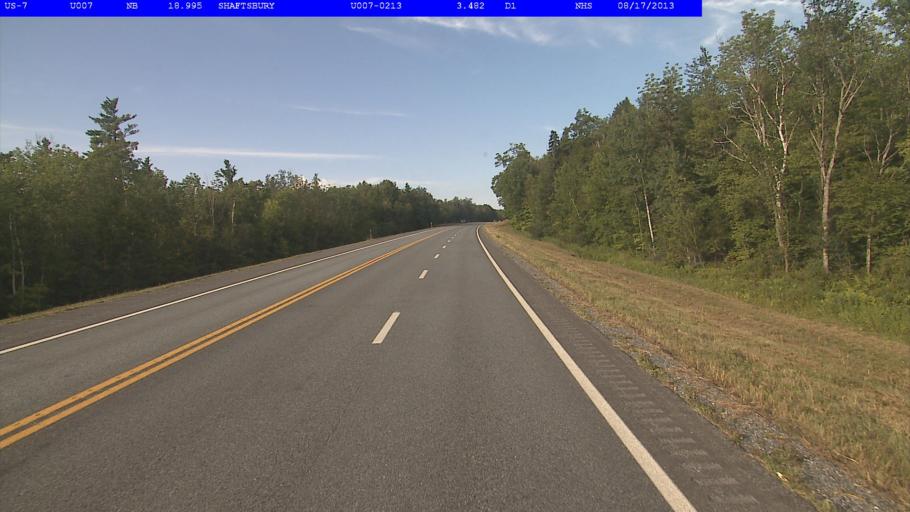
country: US
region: Vermont
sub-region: Bennington County
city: North Bennington
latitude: 42.9771
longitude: -73.1575
